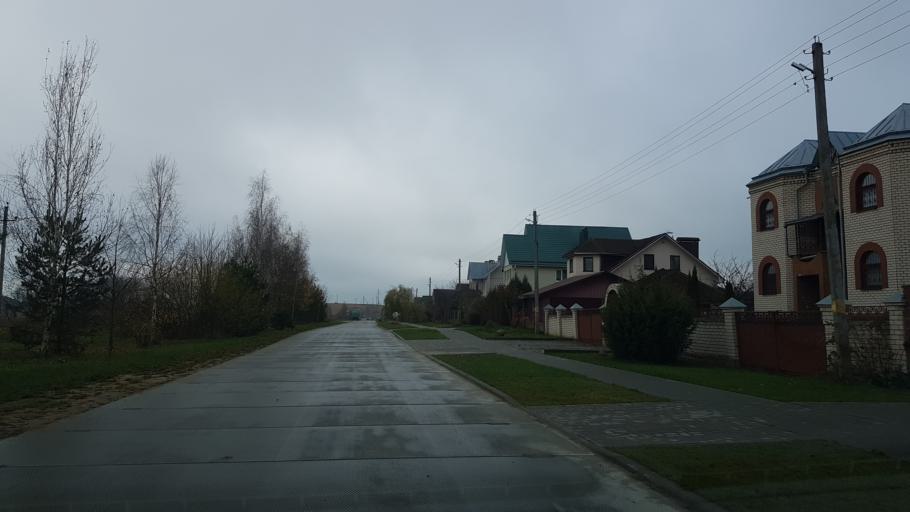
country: BY
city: Fanipol
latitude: 53.7327
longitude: 27.3198
